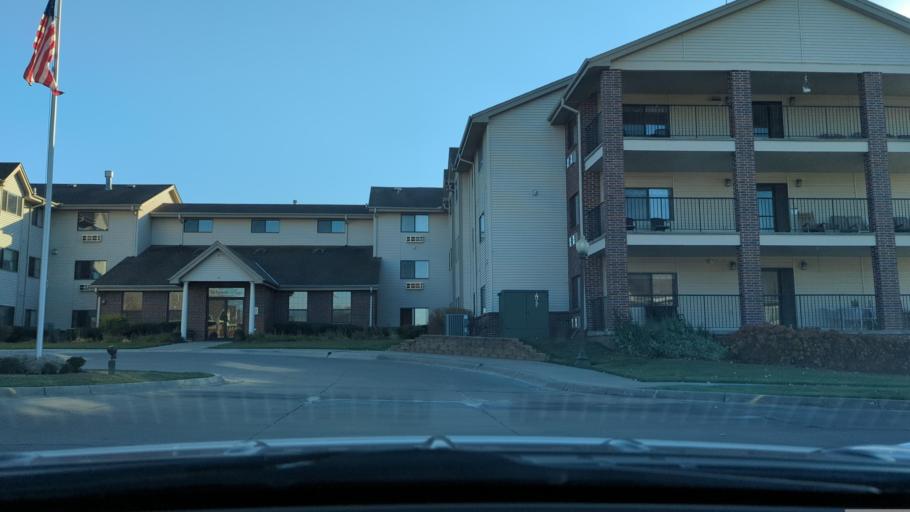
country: US
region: Nebraska
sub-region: Sarpy County
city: Offutt Air Force Base
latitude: 41.1550
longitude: -95.9281
